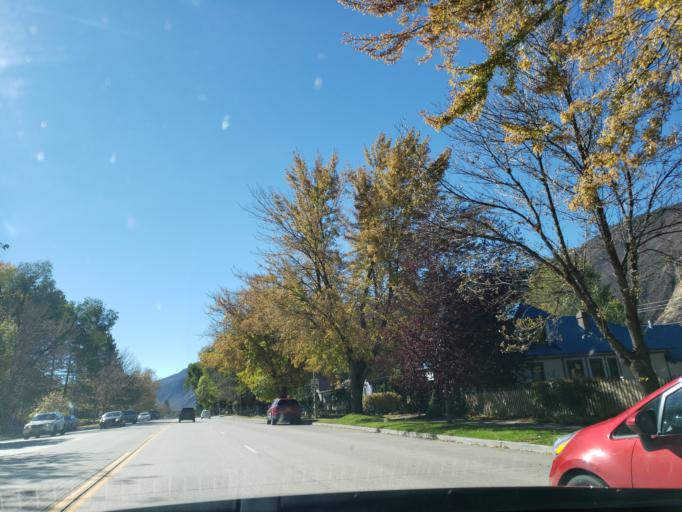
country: US
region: Colorado
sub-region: Garfield County
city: Glenwood Springs
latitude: 39.5423
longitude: -107.3250
